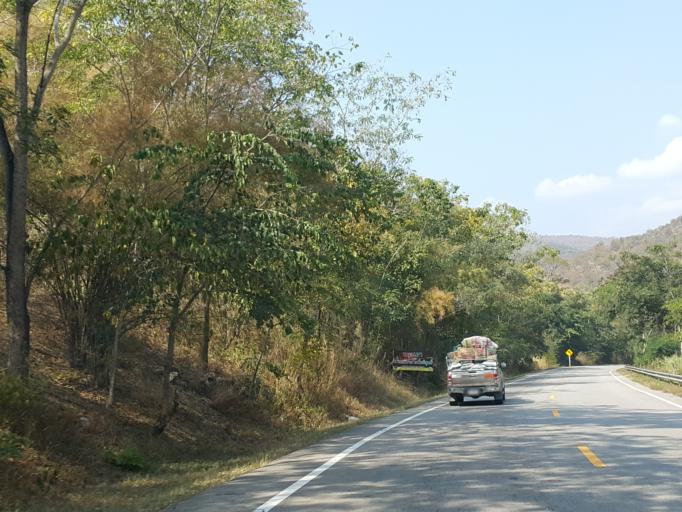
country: TH
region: Chiang Mai
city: Hot
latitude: 18.2309
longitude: 98.5575
